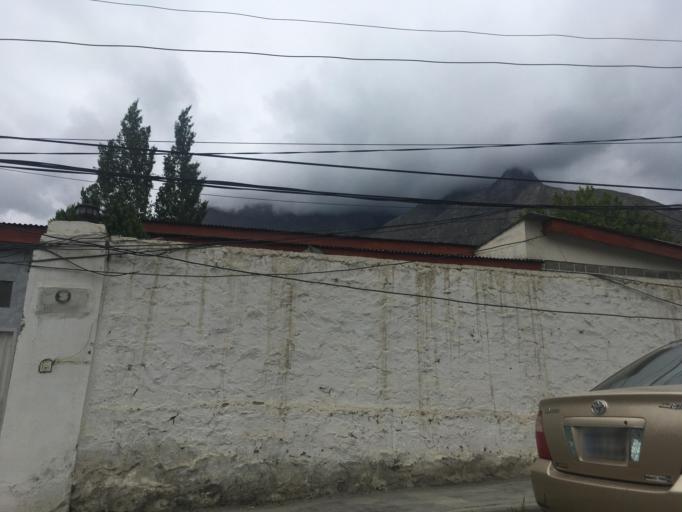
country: PK
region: Gilgit-Baltistan
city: Skardu
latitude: 35.2759
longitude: 75.6364
